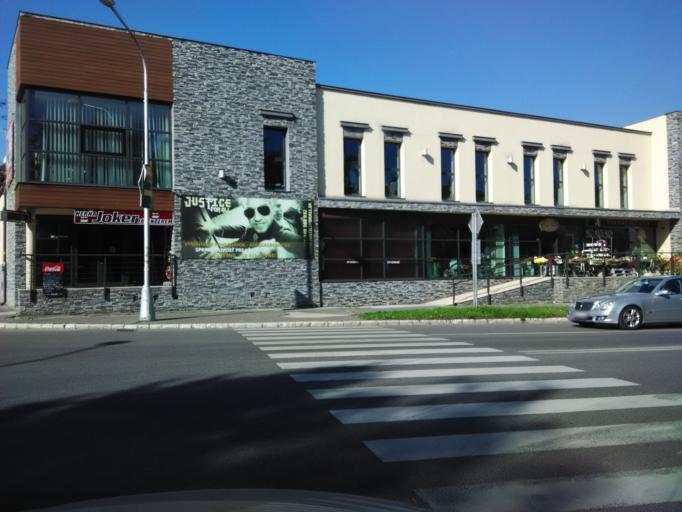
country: SK
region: Nitriansky
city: Komarno
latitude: 47.7582
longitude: 18.1244
